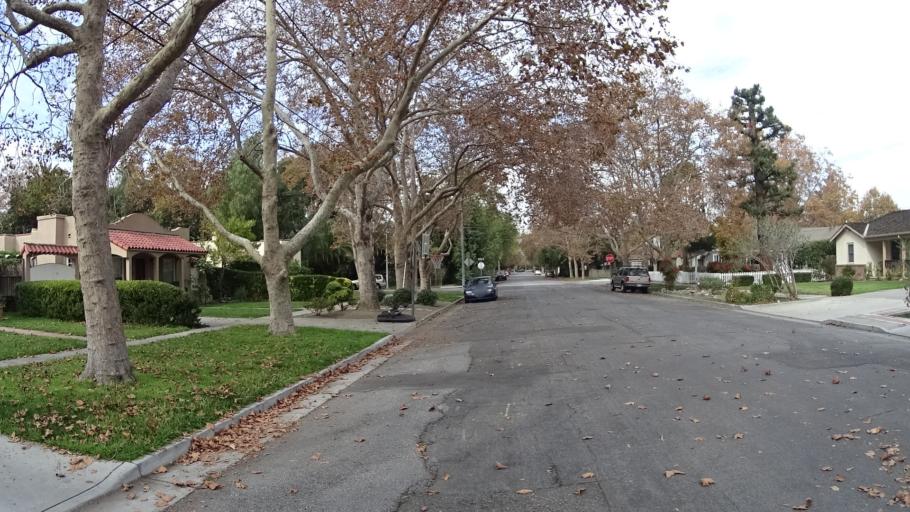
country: US
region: California
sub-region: Santa Clara County
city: Burbank
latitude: 37.3407
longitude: -121.9293
